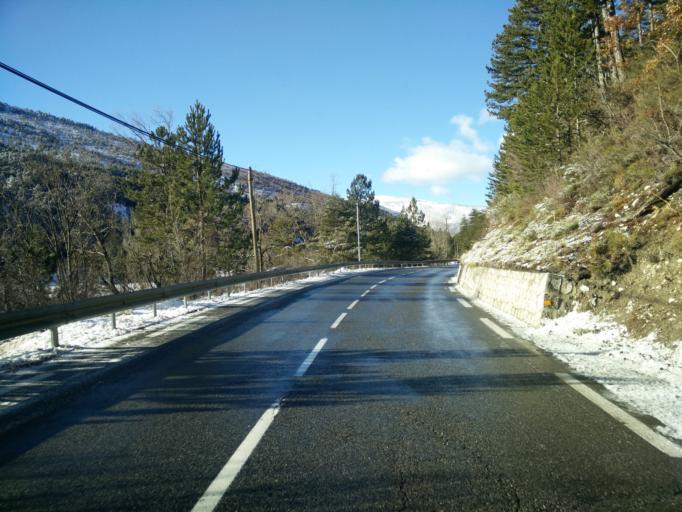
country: FR
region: Provence-Alpes-Cote d'Azur
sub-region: Departement des Alpes-de-Haute-Provence
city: Castellane
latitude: 43.9138
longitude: 6.5762
